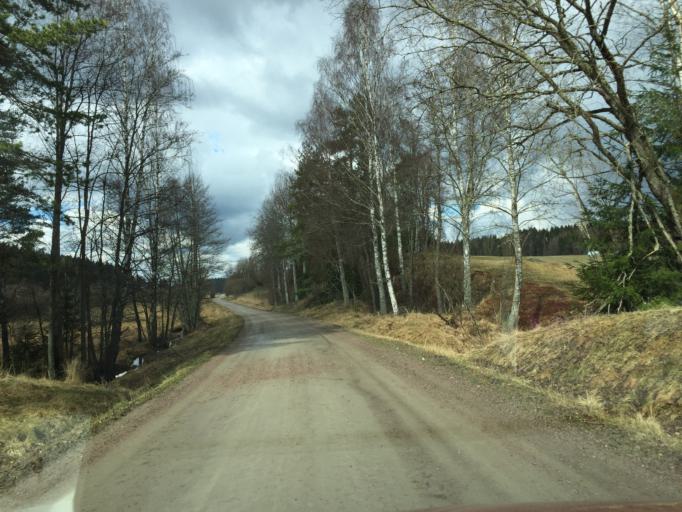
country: SE
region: Soedermanland
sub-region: Nykopings Kommun
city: Nykoping
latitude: 58.9641
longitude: 17.0419
